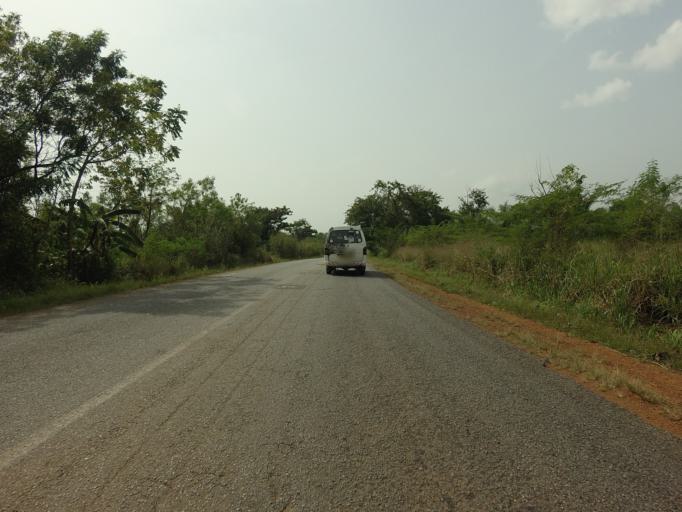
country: GH
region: Volta
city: Ho
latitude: 6.3257
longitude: 0.1638
